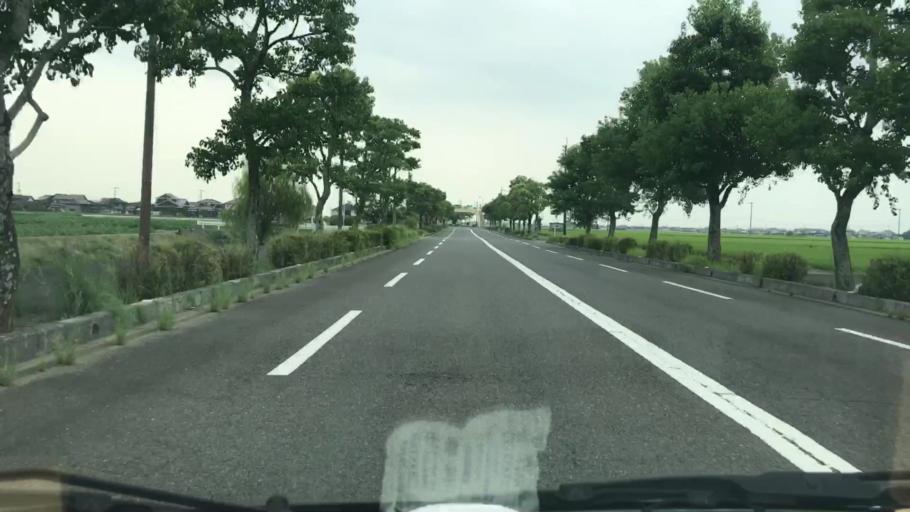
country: JP
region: Saga Prefecture
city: Saga-shi
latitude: 33.2102
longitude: 130.3041
